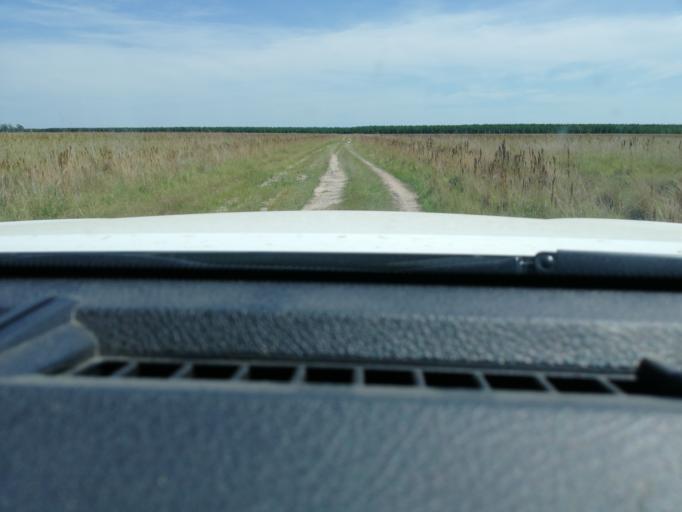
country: AR
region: Corrientes
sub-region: Departamento de San Miguel
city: San Miguel
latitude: -28.0484
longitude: -57.4556
